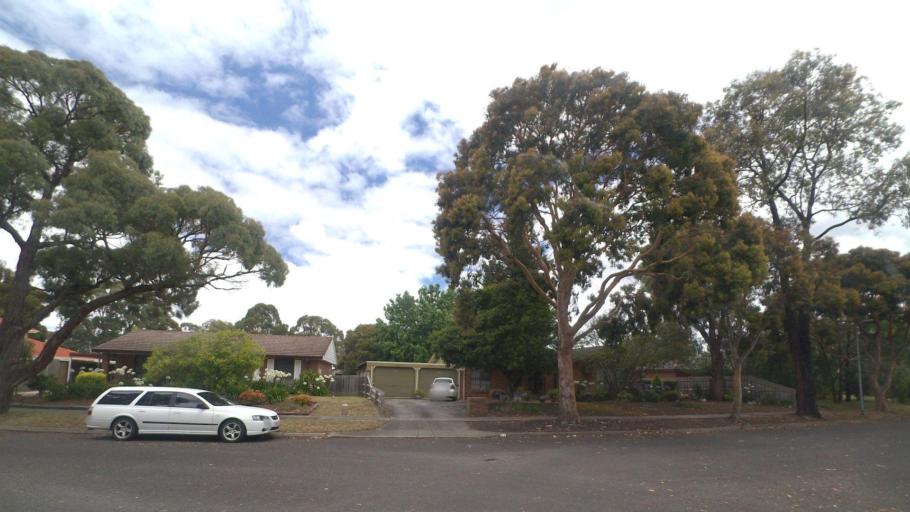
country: AU
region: Victoria
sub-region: Knox
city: Wantirna
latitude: -37.8640
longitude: 145.2294
